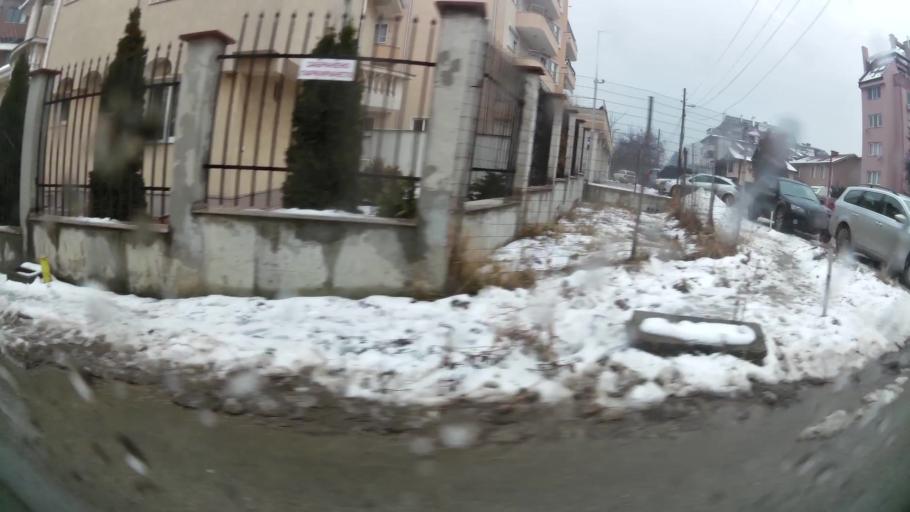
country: BG
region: Sofia-Capital
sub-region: Stolichna Obshtina
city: Sofia
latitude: 42.6784
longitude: 23.2578
